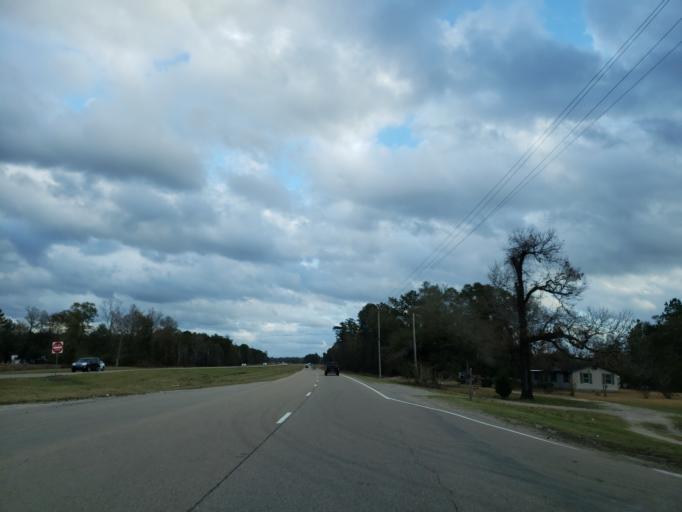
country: US
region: Mississippi
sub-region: Perry County
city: New Augusta
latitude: 31.1268
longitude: -88.8504
